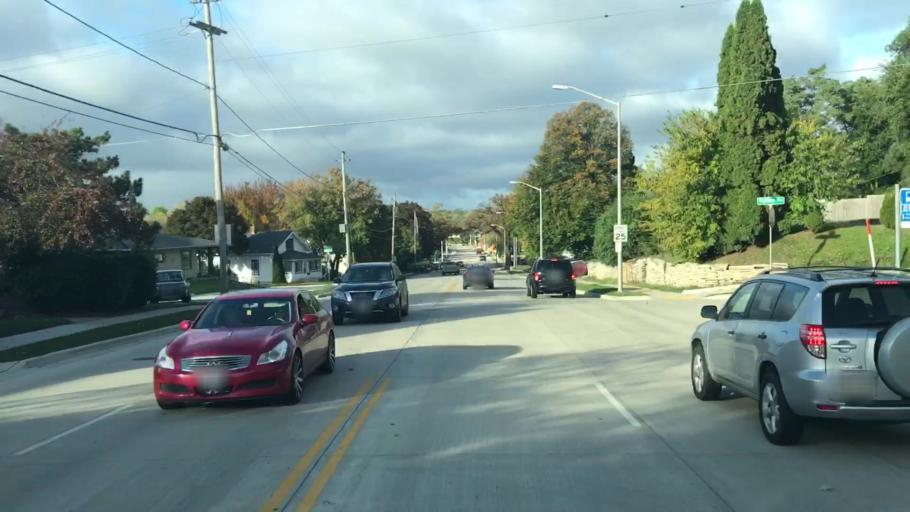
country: US
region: Wisconsin
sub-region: Waukesha County
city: Waukesha
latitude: 43.0235
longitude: -88.2126
